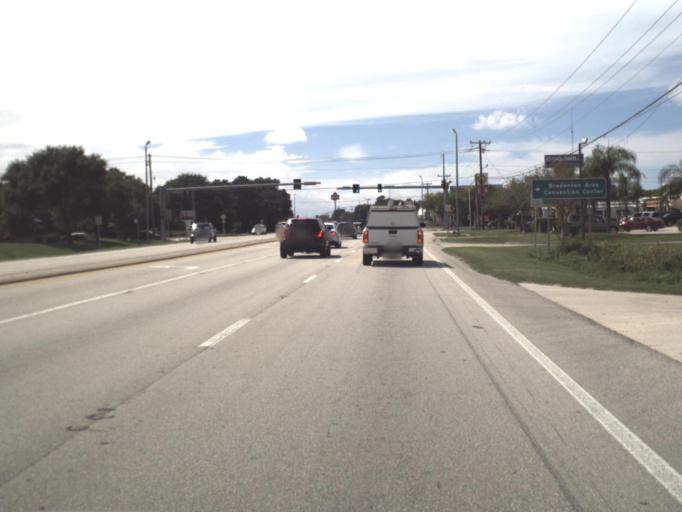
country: US
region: Florida
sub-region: Manatee County
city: Memphis
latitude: 27.5213
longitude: -82.5511
